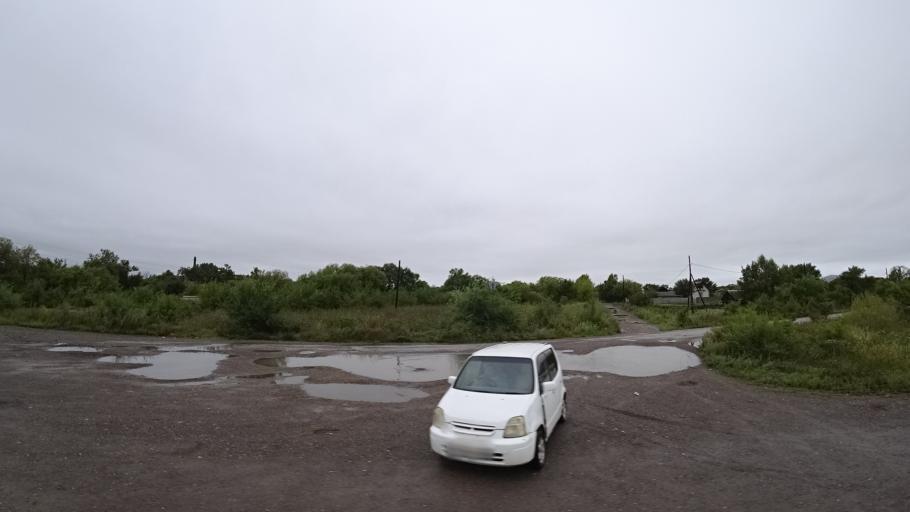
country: RU
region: Primorskiy
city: Monastyrishche
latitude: 44.2134
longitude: 132.4496
